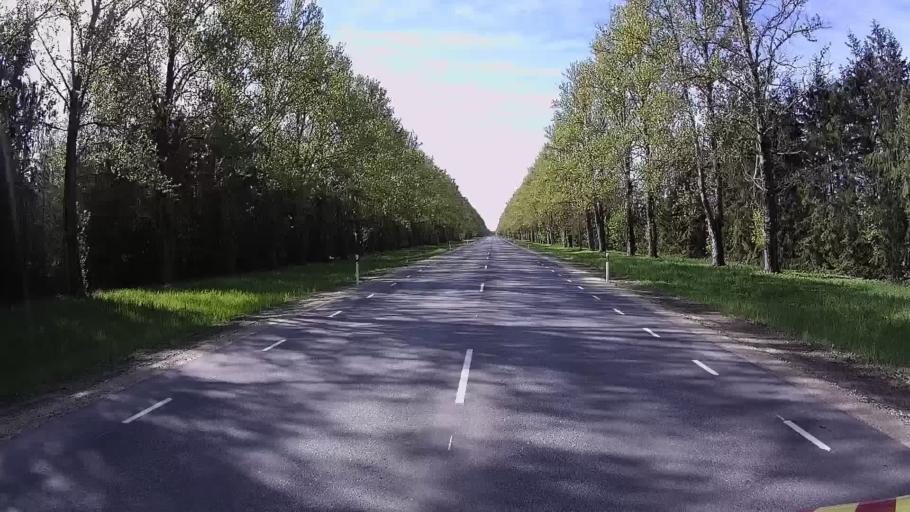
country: EE
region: Polvamaa
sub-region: Polva linn
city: Polva
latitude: 58.2929
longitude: 27.0016
